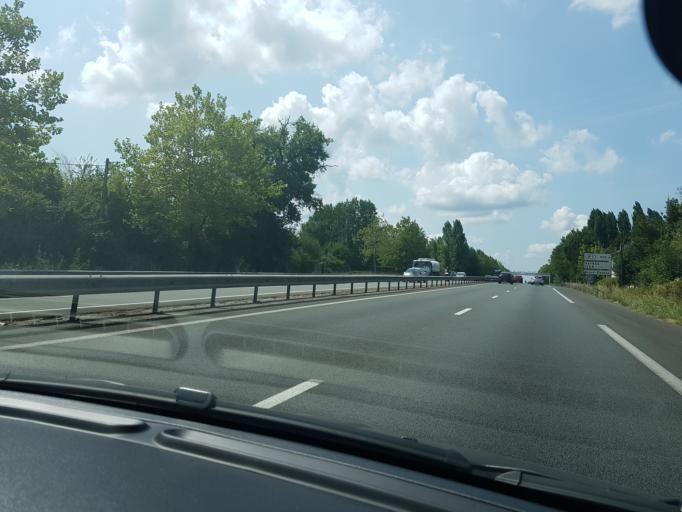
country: FR
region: Aquitaine
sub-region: Departement de la Gironde
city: Vayres
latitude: 44.8840
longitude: -0.3257
